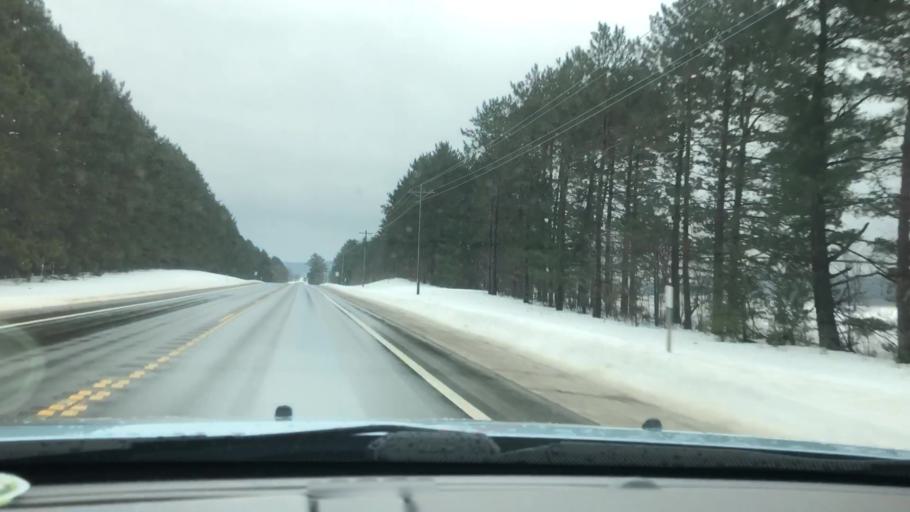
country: US
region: Michigan
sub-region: Charlevoix County
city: Boyne City
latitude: 45.0945
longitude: -84.9687
